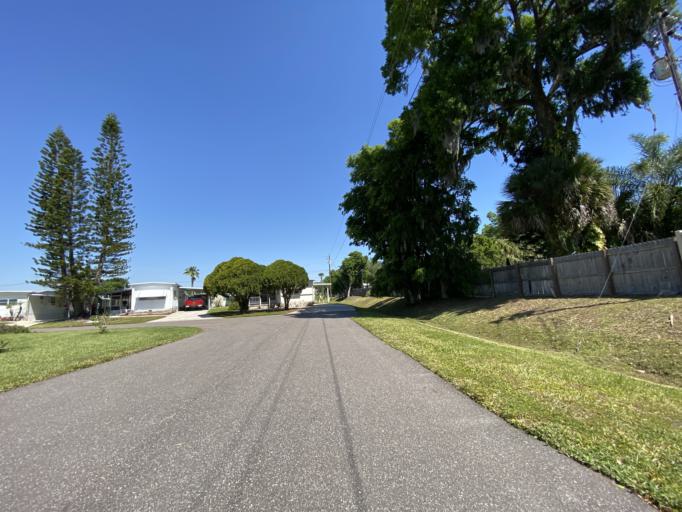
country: US
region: Florida
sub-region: Volusia County
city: South Daytona
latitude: 29.1587
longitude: -81.0167
